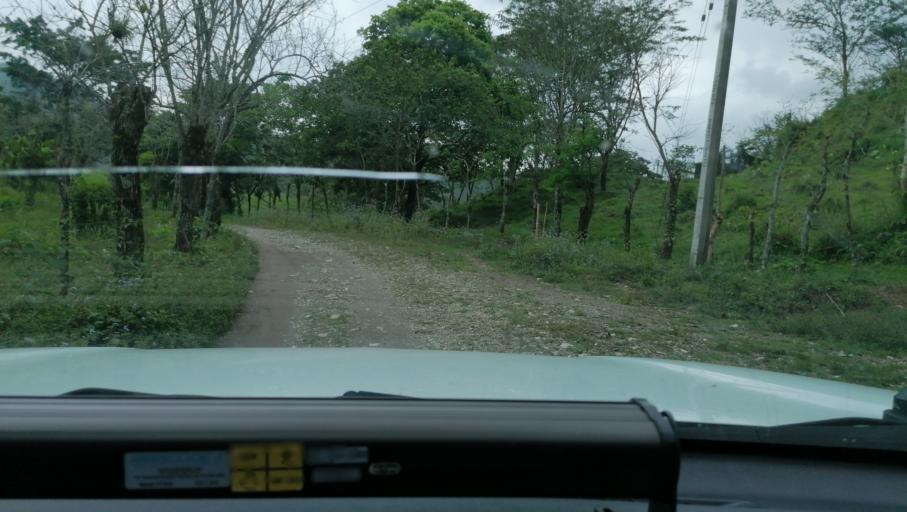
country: MX
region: Chiapas
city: Ixtacomitan
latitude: 17.3684
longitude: -93.1832
